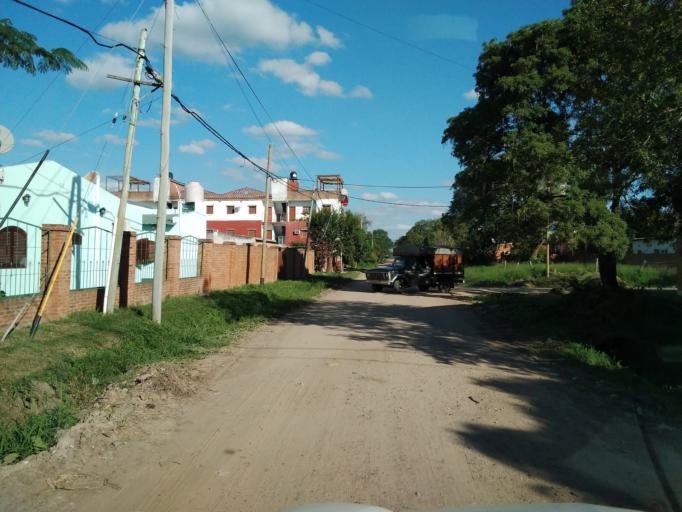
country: AR
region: Corrientes
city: Corrientes
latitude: -27.4608
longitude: -58.7772
